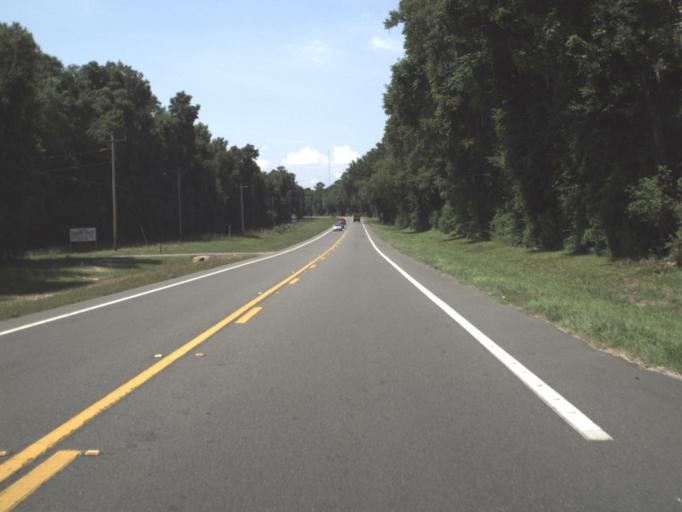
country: US
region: Florida
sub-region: Alachua County
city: Gainesville
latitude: 29.5758
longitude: -82.3926
